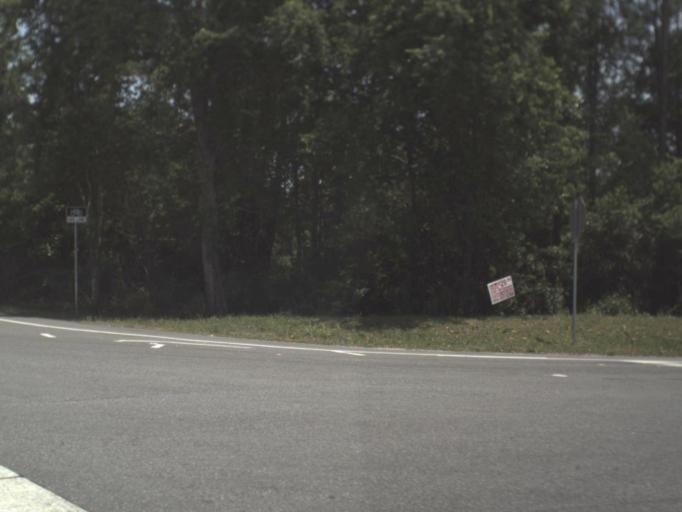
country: US
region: Florida
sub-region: Duval County
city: Baldwin
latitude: 30.2042
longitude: -81.9913
